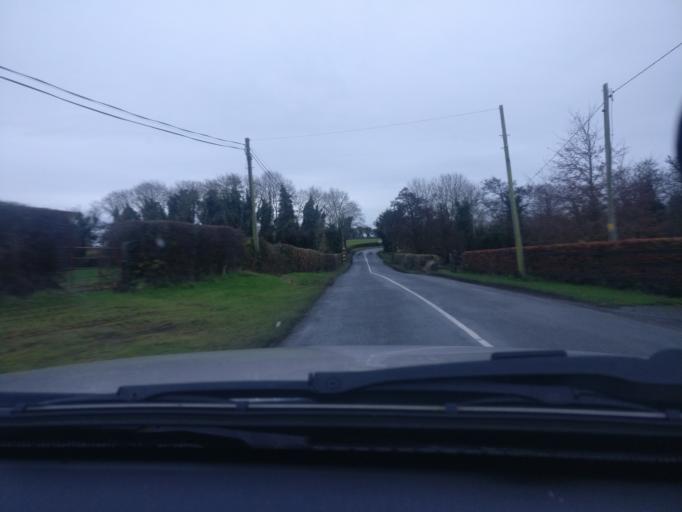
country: IE
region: Leinster
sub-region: An Mhi
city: Dunshaughlin
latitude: 53.4956
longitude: -6.6029
